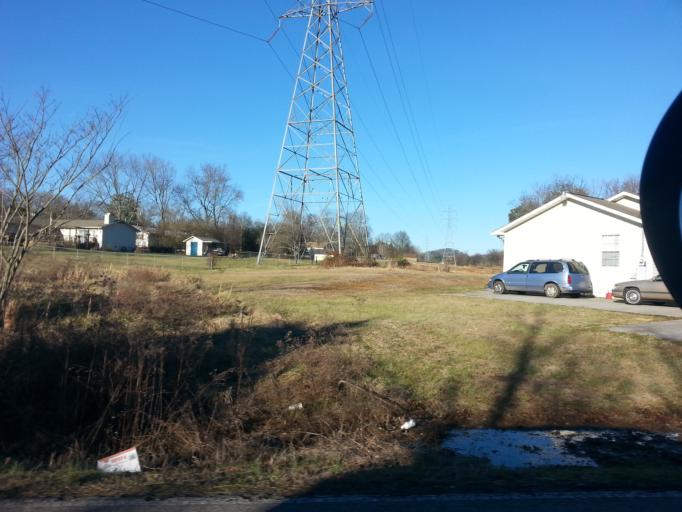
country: US
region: Tennessee
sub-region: Blount County
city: Eagleton Village
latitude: 35.8740
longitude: -83.9349
